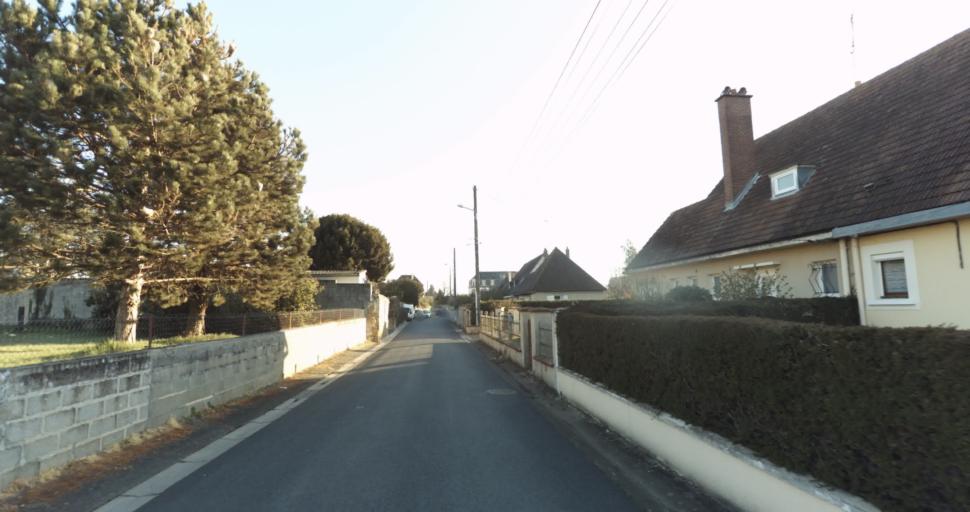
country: FR
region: Lower Normandy
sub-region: Departement du Calvados
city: Saint-Pierre-sur-Dives
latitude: 49.0215
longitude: -0.0407
